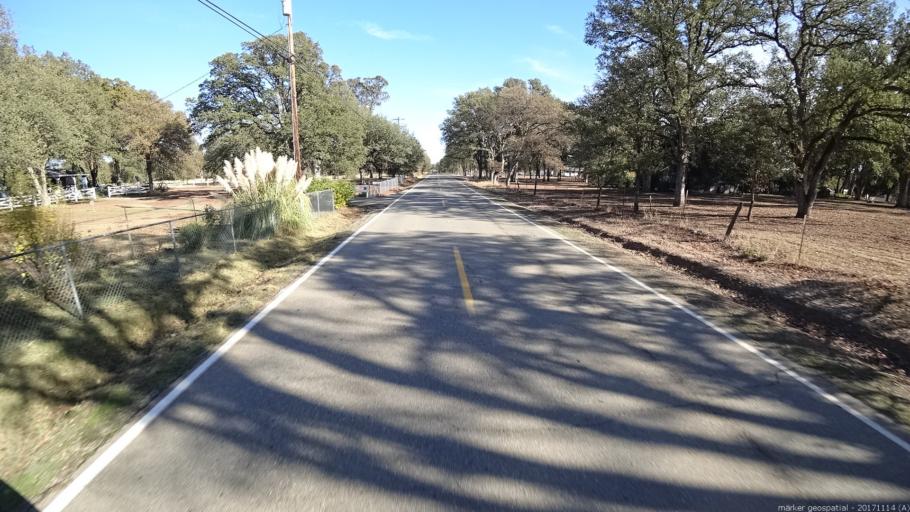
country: US
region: California
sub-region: Shasta County
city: Anderson
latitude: 40.3883
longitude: -122.4534
